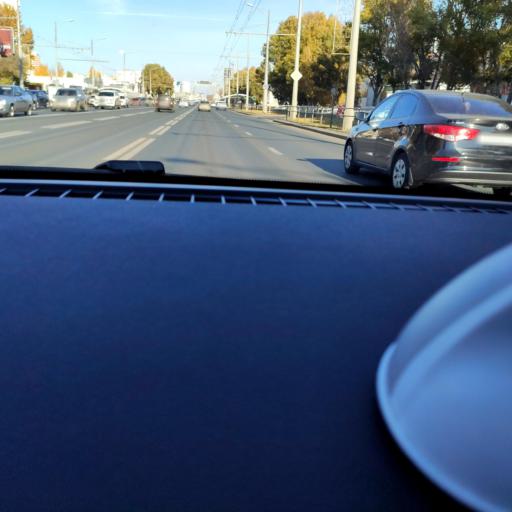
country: RU
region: Samara
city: Samara
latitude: 53.2458
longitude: 50.2140
